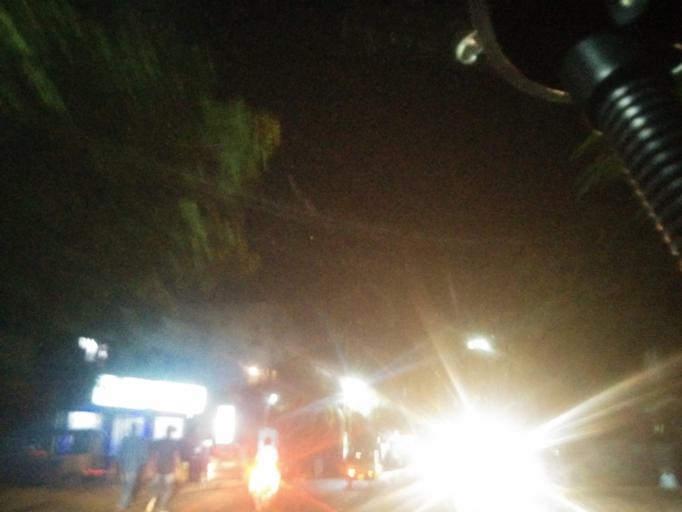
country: IN
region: Andhra Pradesh
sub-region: East Godavari
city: Rajahmundry
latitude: 17.0104
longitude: 81.7787
